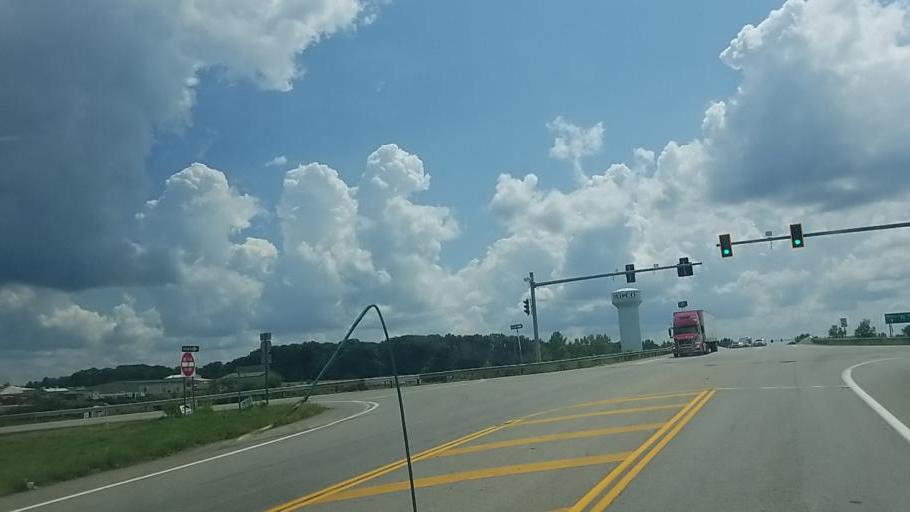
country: US
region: Ohio
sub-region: Delaware County
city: Ashley
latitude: 40.3758
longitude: -82.8292
